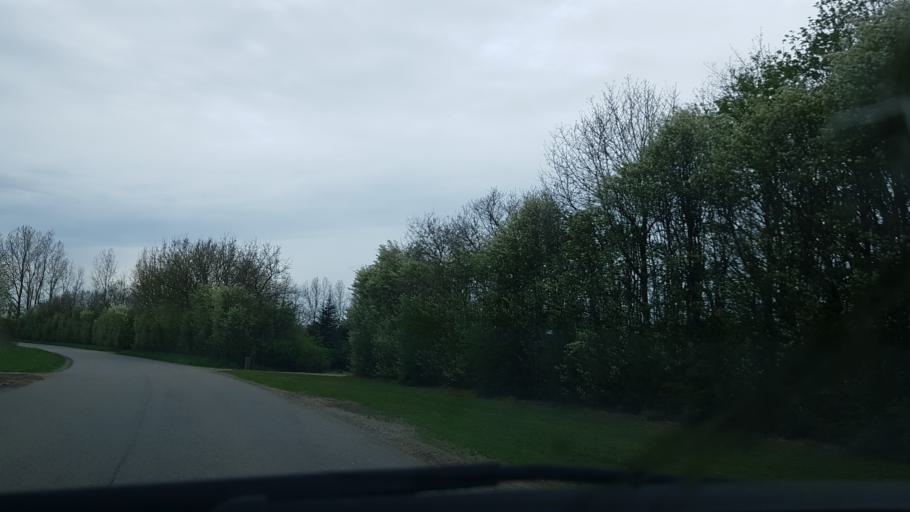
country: DK
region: South Denmark
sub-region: Kolding Kommune
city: Vamdrup
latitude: 55.4407
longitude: 9.3012
